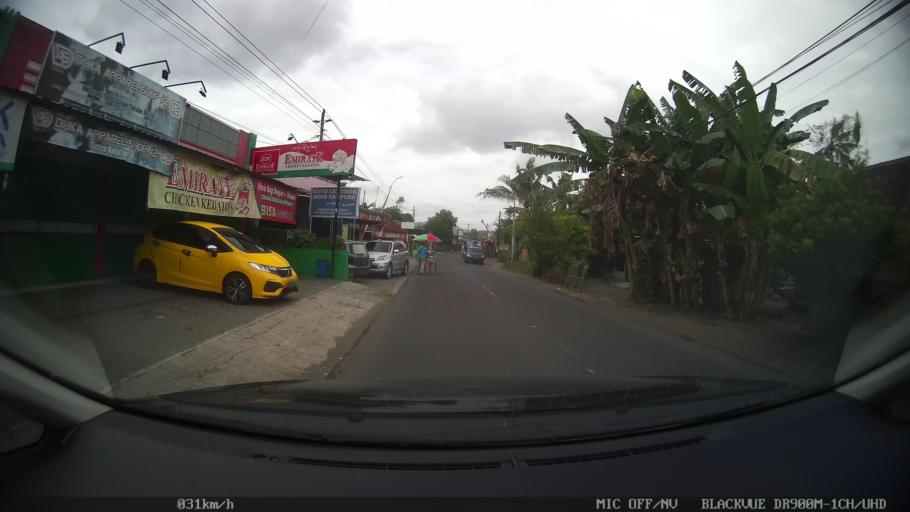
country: ID
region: Daerah Istimewa Yogyakarta
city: Sewon
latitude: -7.8697
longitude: 110.4074
